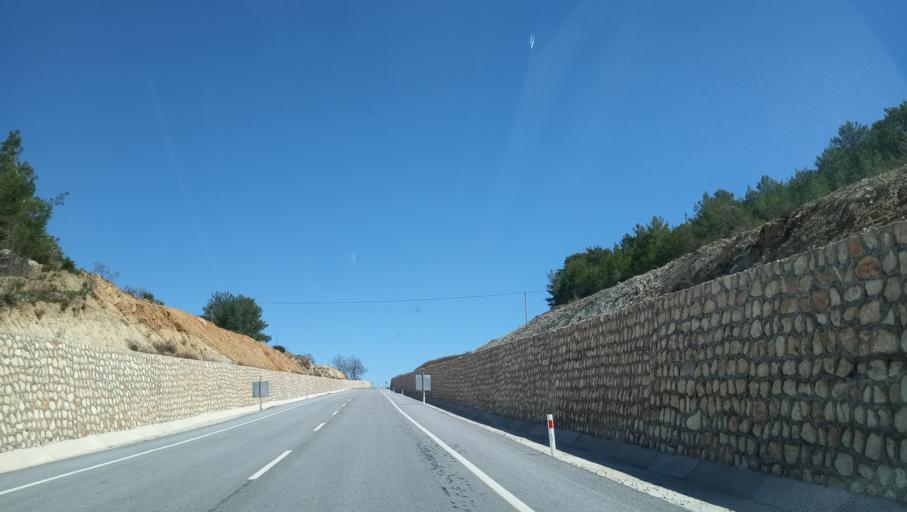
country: TR
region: Antalya
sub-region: Alanya
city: Okurcalar
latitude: 36.7750
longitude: 31.7615
